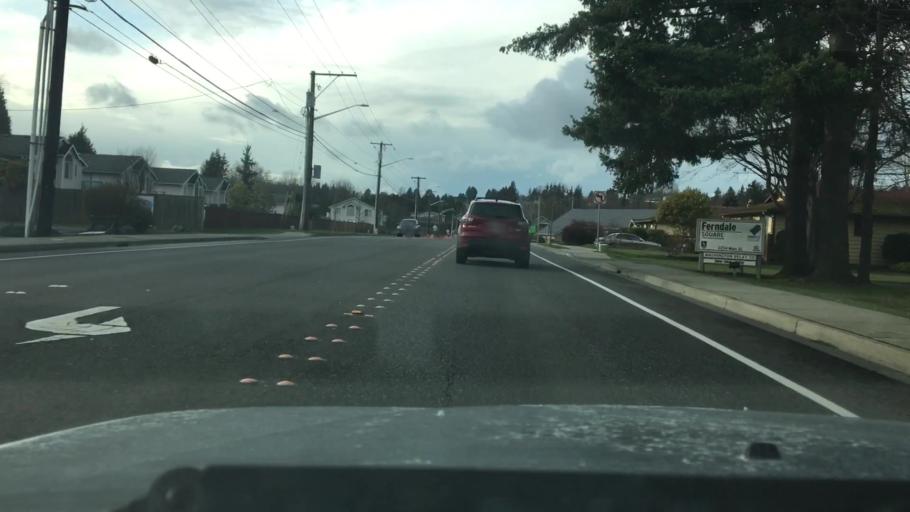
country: US
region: Washington
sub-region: Whatcom County
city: Ferndale
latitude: 48.8484
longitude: -122.6041
